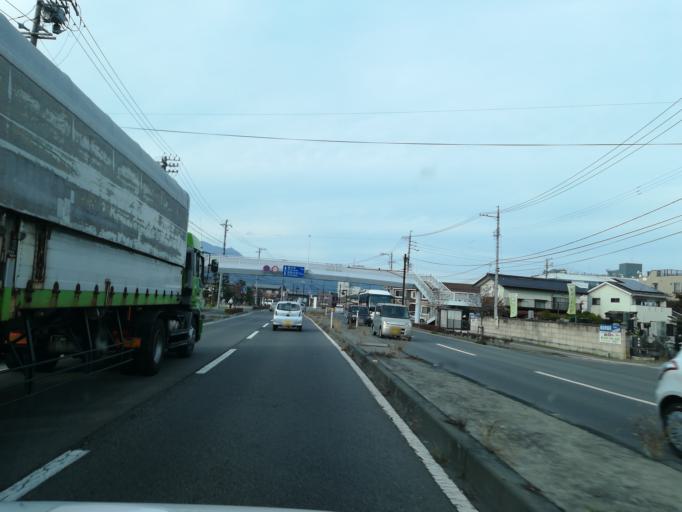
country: JP
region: Nagano
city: Nagano-shi
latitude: 36.6063
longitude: 138.1787
